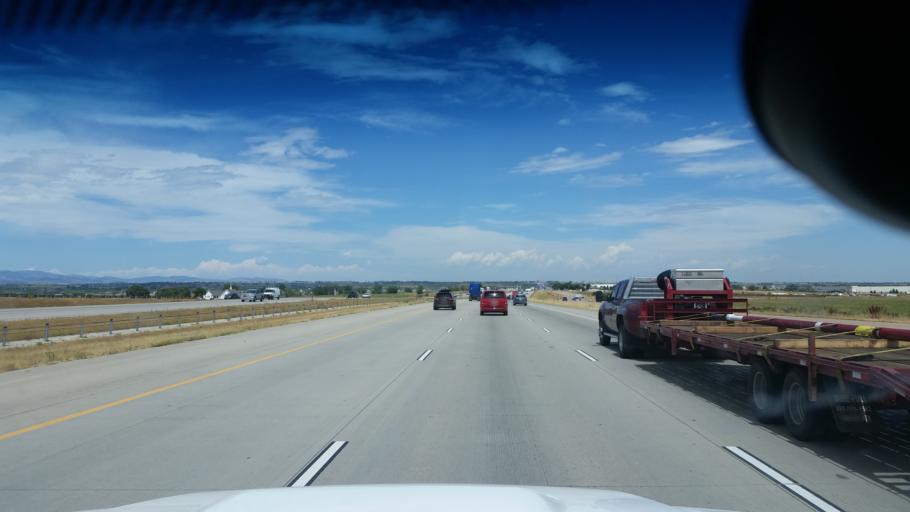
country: US
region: Colorado
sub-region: Weld County
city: Firestone
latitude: 40.1251
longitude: -104.9799
